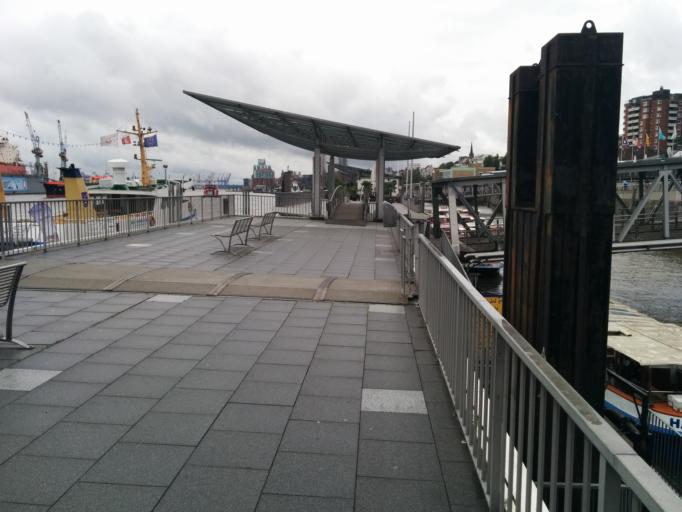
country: DE
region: Hamburg
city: St. Pauli
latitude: 53.5453
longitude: 9.9669
